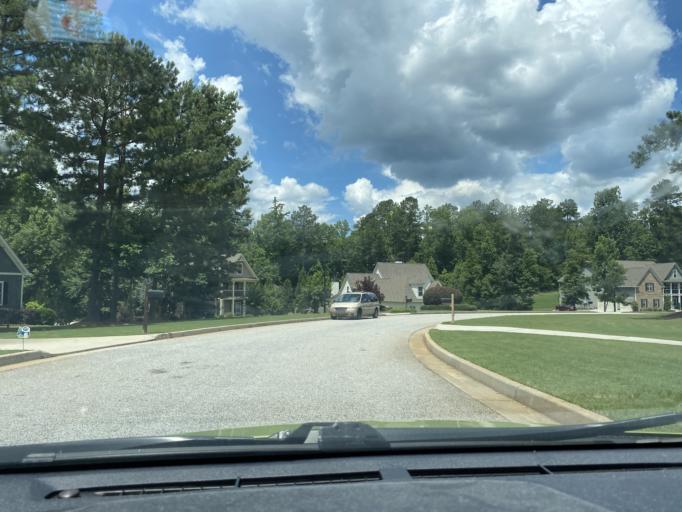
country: US
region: Georgia
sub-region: Fayette County
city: Peachtree City
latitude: 33.4252
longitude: -84.6690
